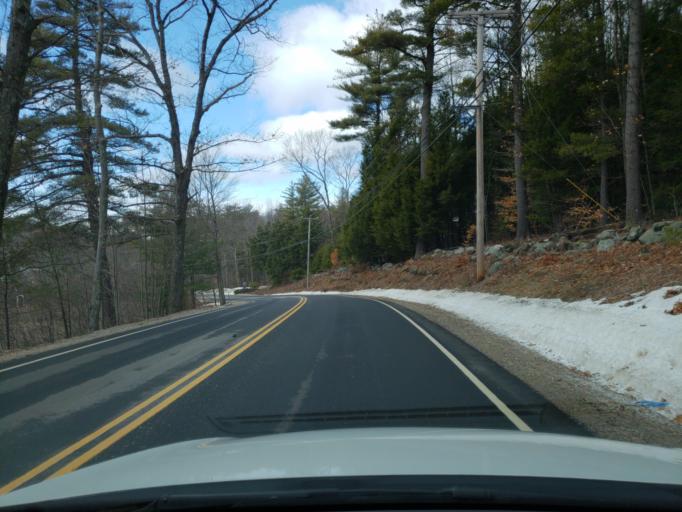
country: US
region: New Hampshire
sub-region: Hillsborough County
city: Greenfield
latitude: 43.0128
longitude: -71.8745
